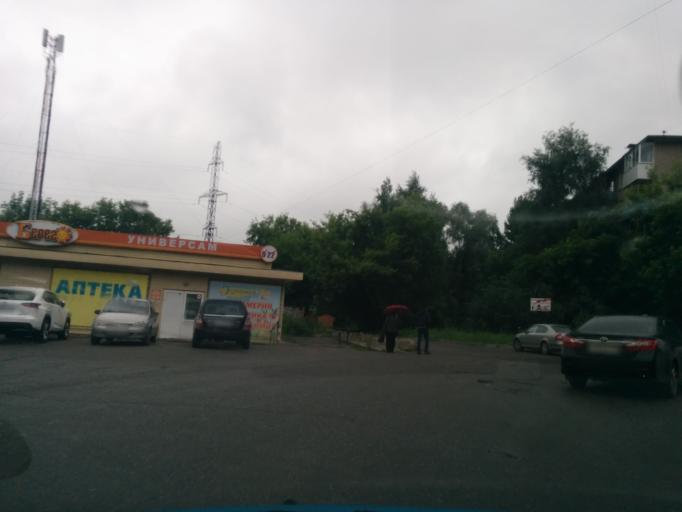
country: RU
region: Perm
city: Perm
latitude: 57.9898
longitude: 56.2336
